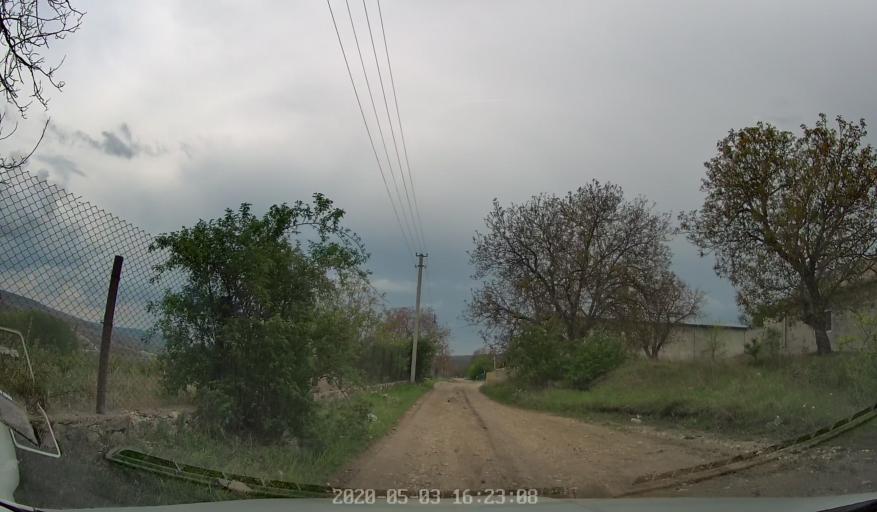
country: MD
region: Calarasi
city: Calarasi
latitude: 47.1982
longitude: 28.3480
